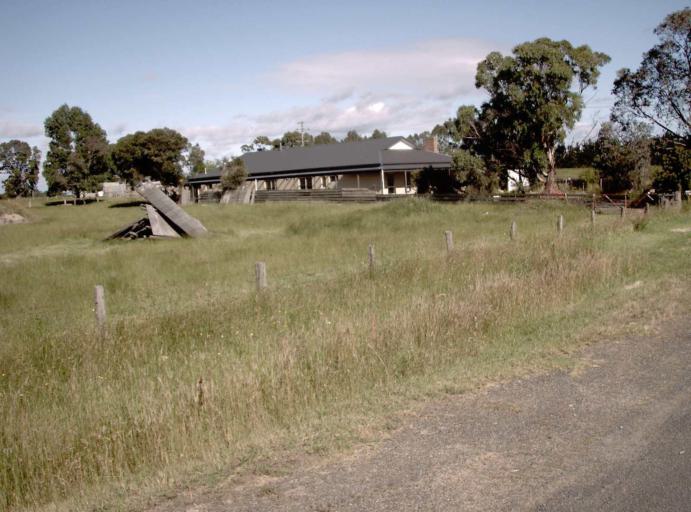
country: AU
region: Victoria
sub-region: Latrobe
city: Traralgon
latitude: -38.1825
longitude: 146.5004
